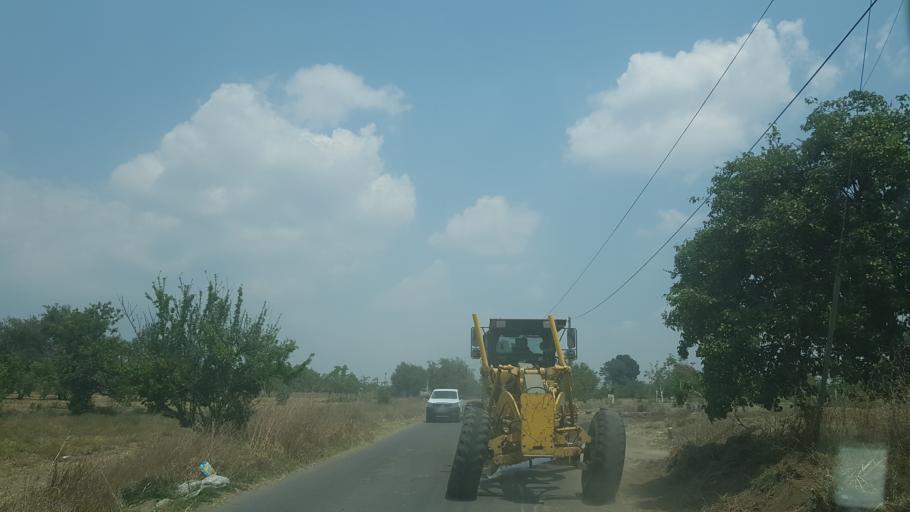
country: MX
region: Puebla
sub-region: San Nicolas de los Ranchos
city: San Pedro Yancuitlalpan
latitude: 19.0861
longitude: -98.4815
